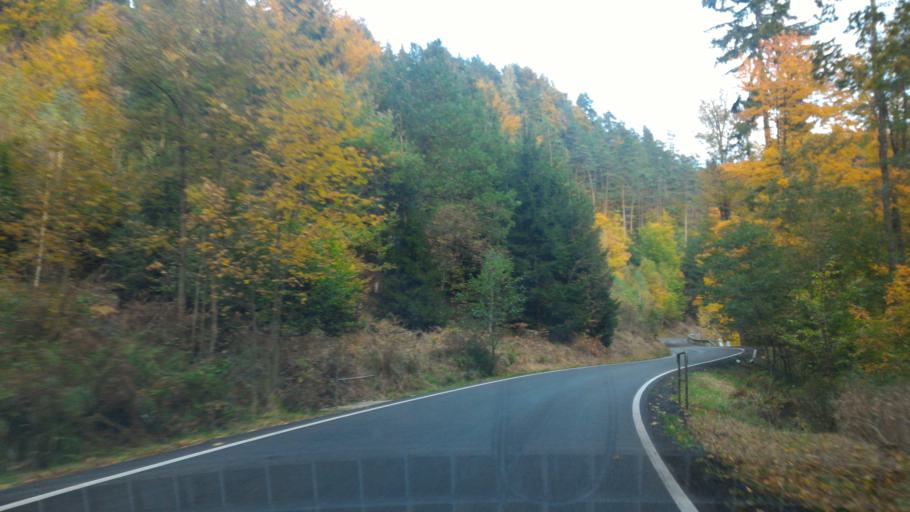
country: CZ
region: Ustecky
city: Ceska Kamenice
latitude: 50.8059
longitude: 14.4524
